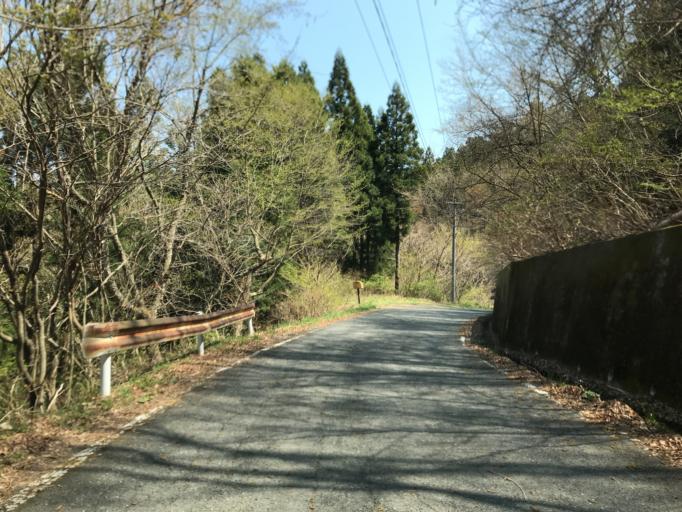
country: JP
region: Fukushima
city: Ishikawa
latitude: 36.9933
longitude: 140.6050
